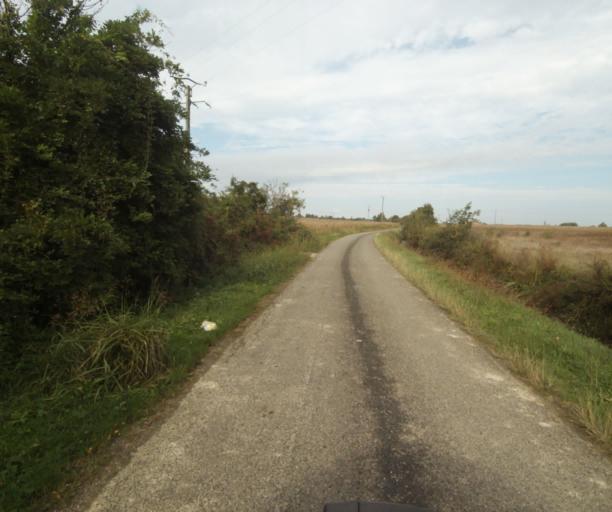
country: FR
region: Midi-Pyrenees
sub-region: Departement du Tarn-et-Garonne
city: Finhan
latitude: 43.9152
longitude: 1.2376
